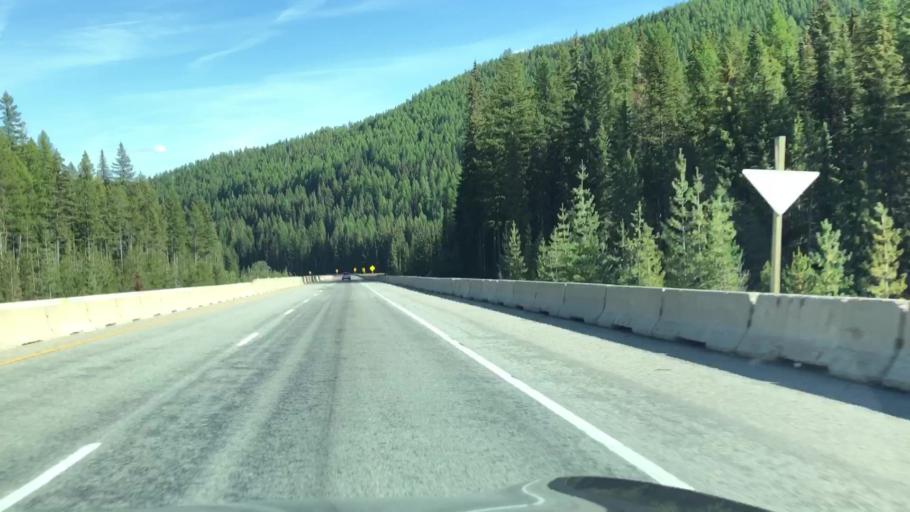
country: US
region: Idaho
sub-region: Shoshone County
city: Wallace
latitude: 47.4355
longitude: -115.6767
